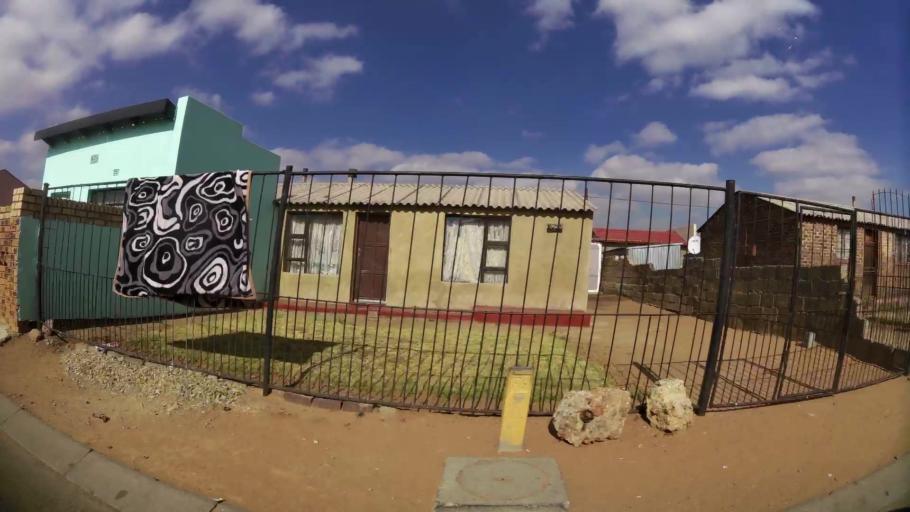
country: ZA
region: Gauteng
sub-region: City of Johannesburg Metropolitan Municipality
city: Roodepoort
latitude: -26.2152
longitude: 27.8993
